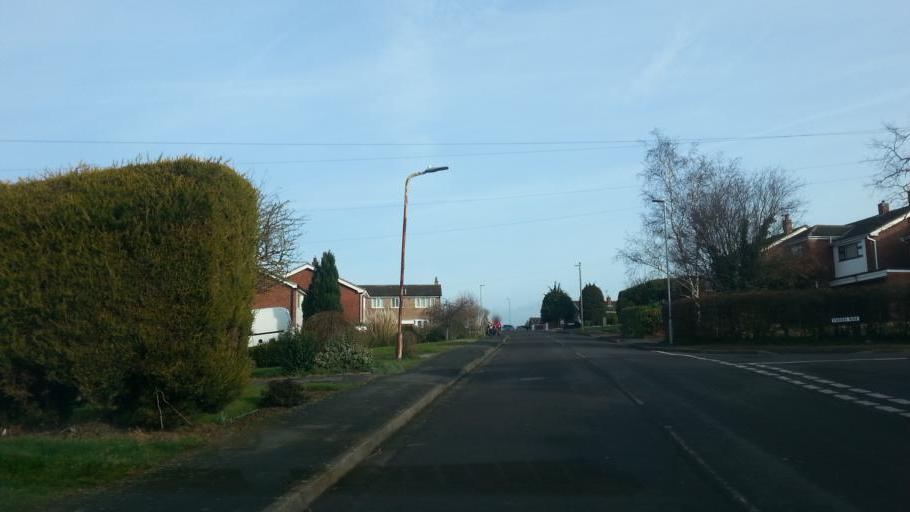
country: GB
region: England
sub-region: Leicestershire
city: Melton Mowbray
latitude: 52.7547
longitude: -0.8944
